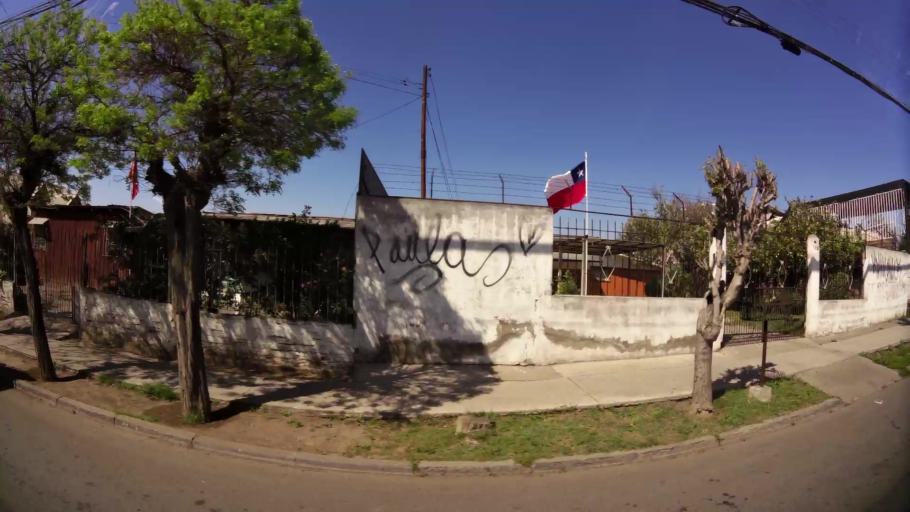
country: CL
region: Santiago Metropolitan
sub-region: Provincia de Santiago
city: Lo Prado
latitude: -33.4978
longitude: -70.7283
